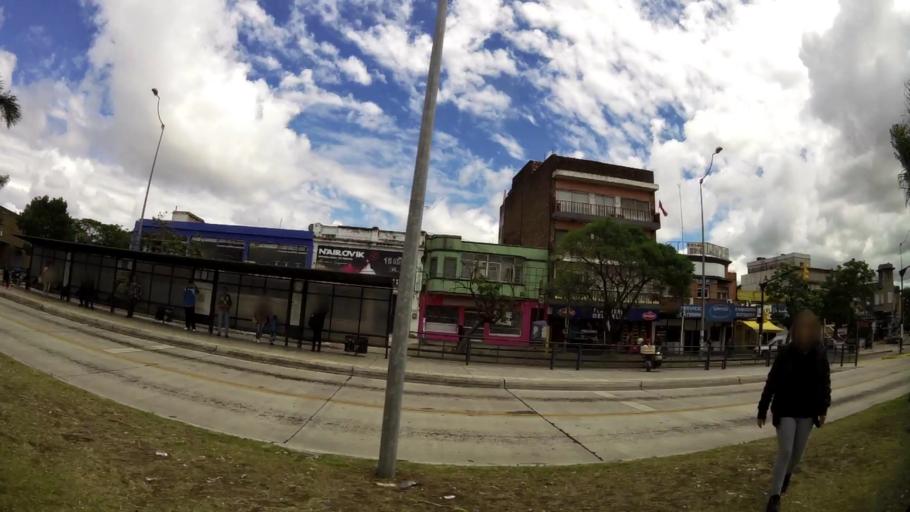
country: UY
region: Montevideo
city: Montevideo
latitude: -34.8543
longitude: -56.1619
